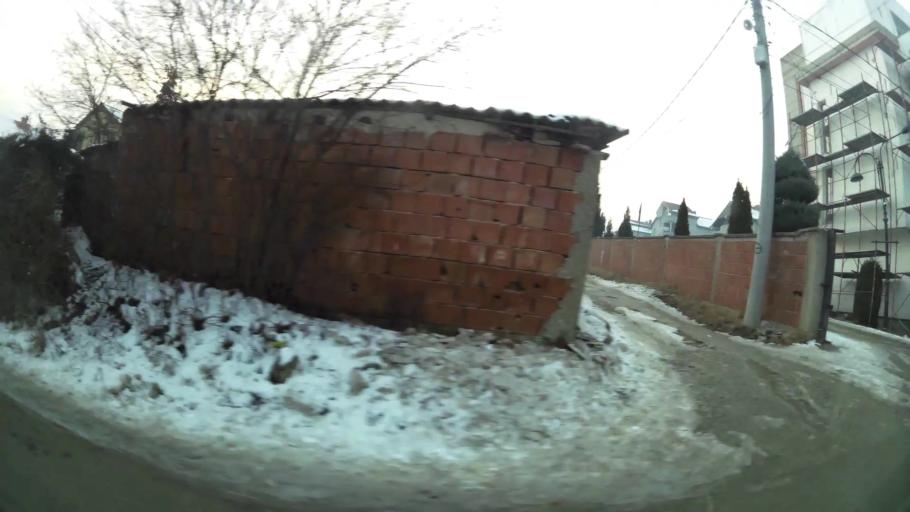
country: MK
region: Suto Orizari
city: Suto Orizare
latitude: 42.0326
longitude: 21.4164
